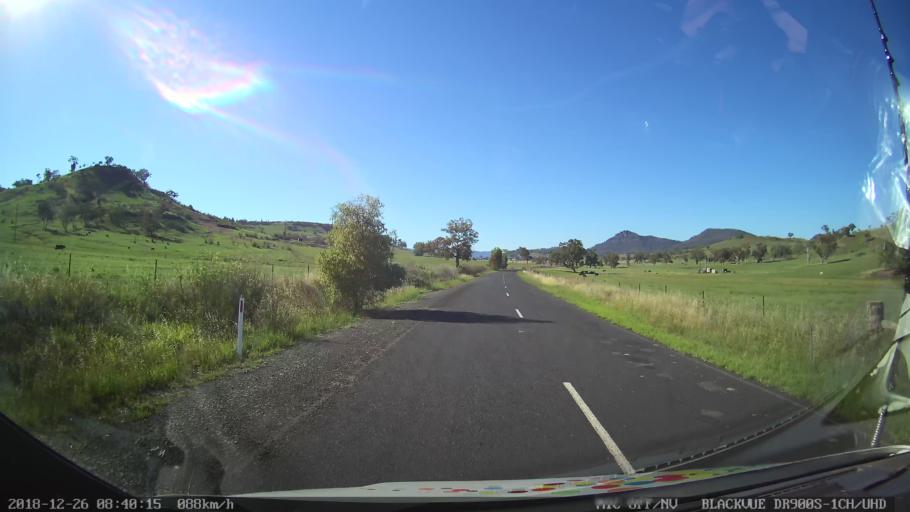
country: AU
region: New South Wales
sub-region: Mid-Western Regional
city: Kandos
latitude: -32.4645
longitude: 150.0762
